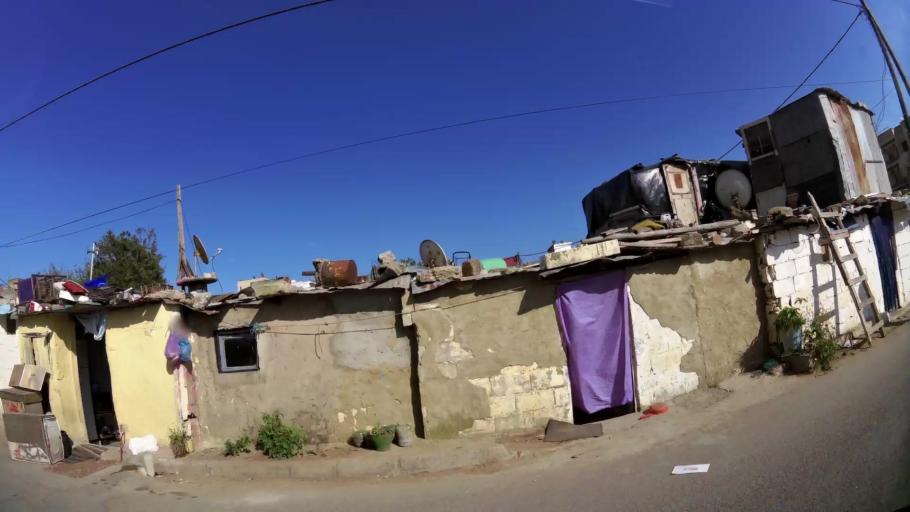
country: MA
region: Rabat-Sale-Zemmour-Zaer
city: Sale
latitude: 34.0458
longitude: -6.8147
